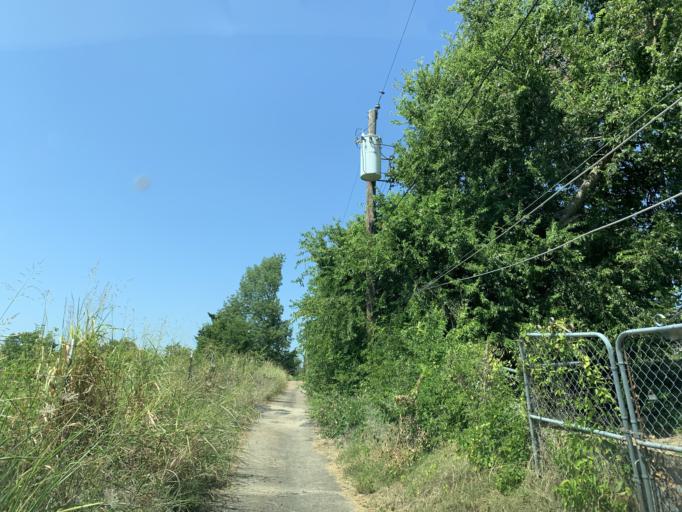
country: US
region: Texas
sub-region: Dallas County
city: Hutchins
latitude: 32.6732
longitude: -96.7499
